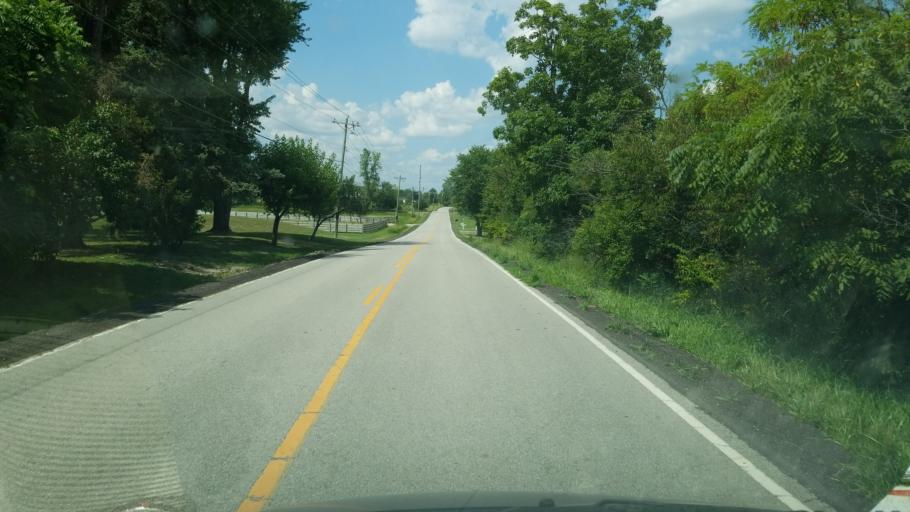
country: US
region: Ohio
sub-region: Champaign County
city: North Lewisburg
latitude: 40.3181
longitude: -83.4741
